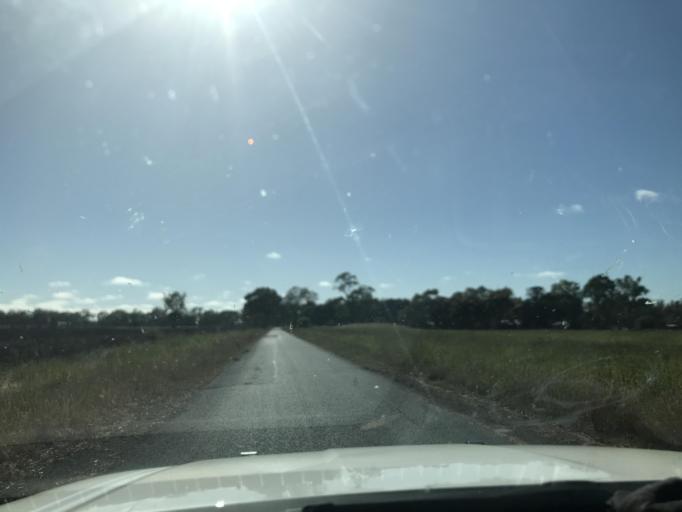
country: AU
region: Victoria
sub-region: Horsham
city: Horsham
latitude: -37.0308
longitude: 141.7215
